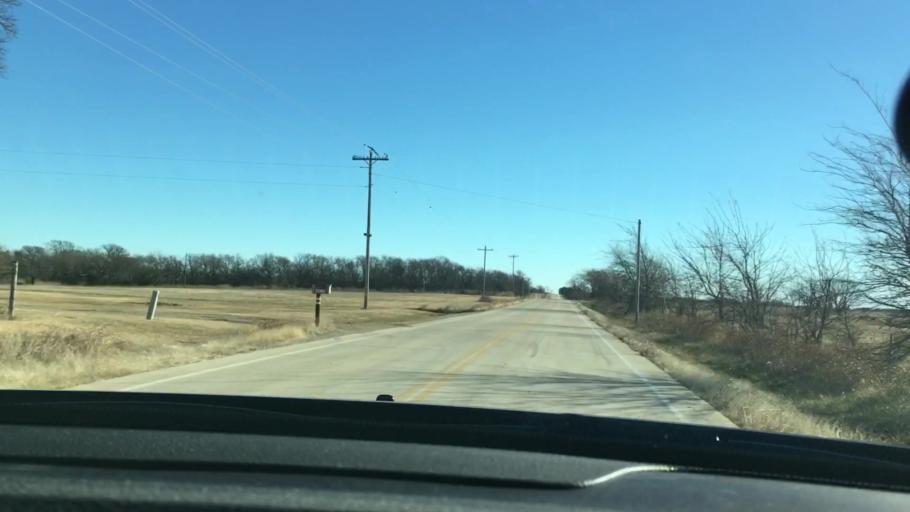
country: US
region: Oklahoma
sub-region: Marshall County
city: Madill
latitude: 34.1144
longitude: -96.6823
